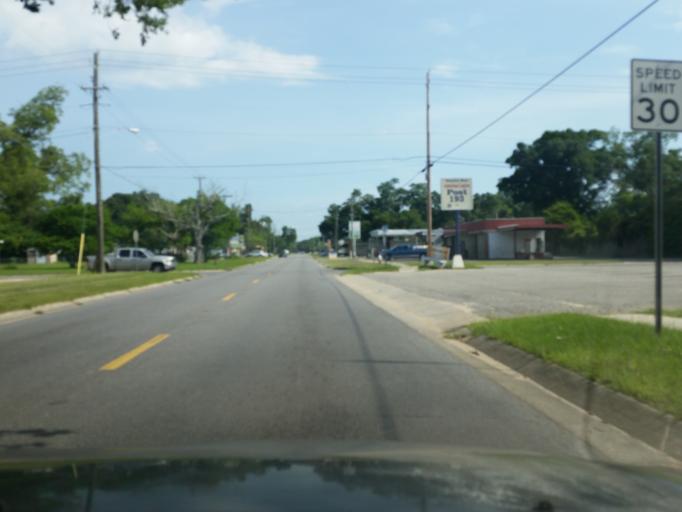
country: US
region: Florida
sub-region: Escambia County
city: Goulding
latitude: 30.4424
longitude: -87.2068
